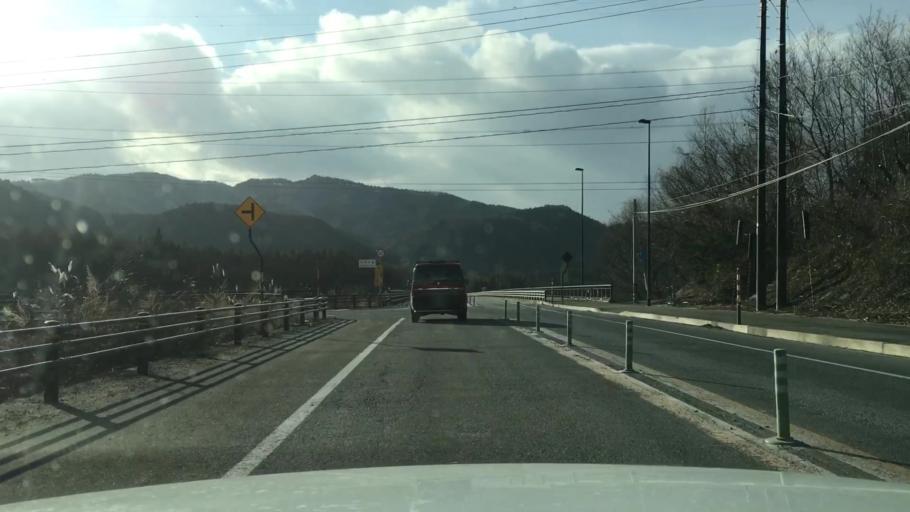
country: JP
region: Iwate
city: Morioka-shi
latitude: 39.6684
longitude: 141.2521
